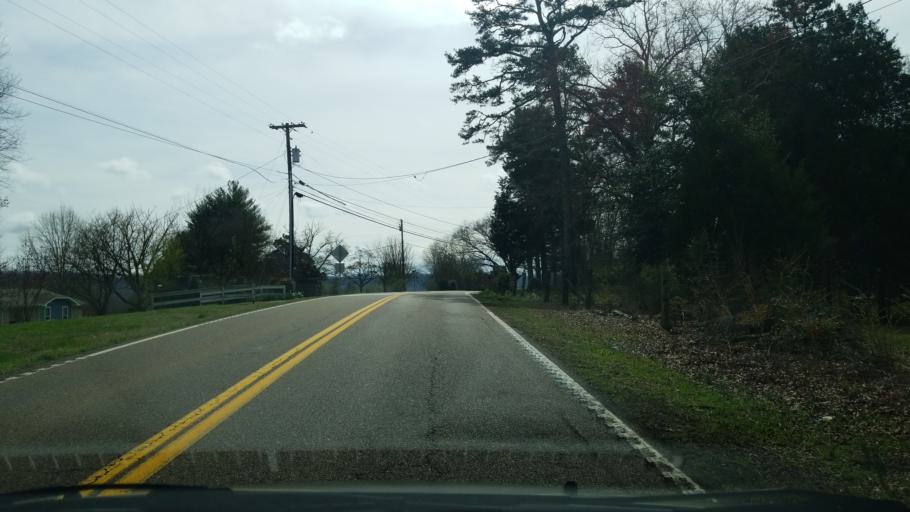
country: US
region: Tennessee
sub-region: Hamilton County
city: Collegedale
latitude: 35.1193
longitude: -85.0686
